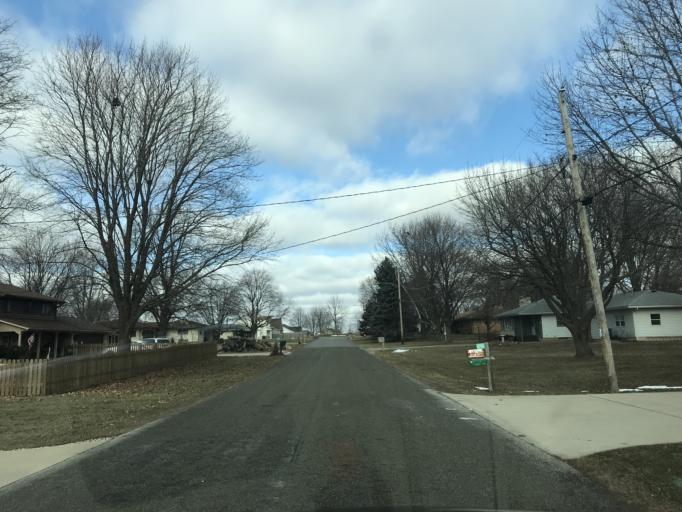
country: US
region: Wisconsin
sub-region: Dane County
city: Monona
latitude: 43.1087
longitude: -89.2899
